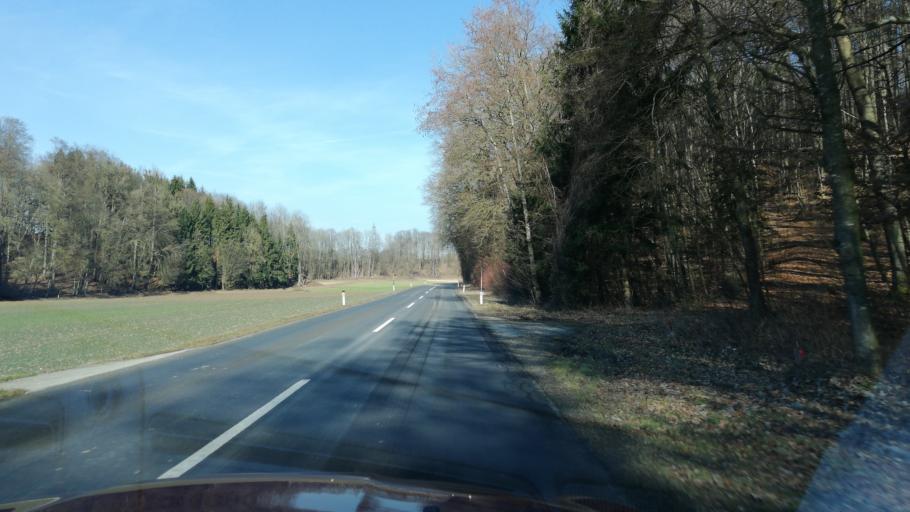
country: AT
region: Upper Austria
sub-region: Politischer Bezirk Vocklabruck
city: Desselbrunn
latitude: 48.0297
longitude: 13.7743
